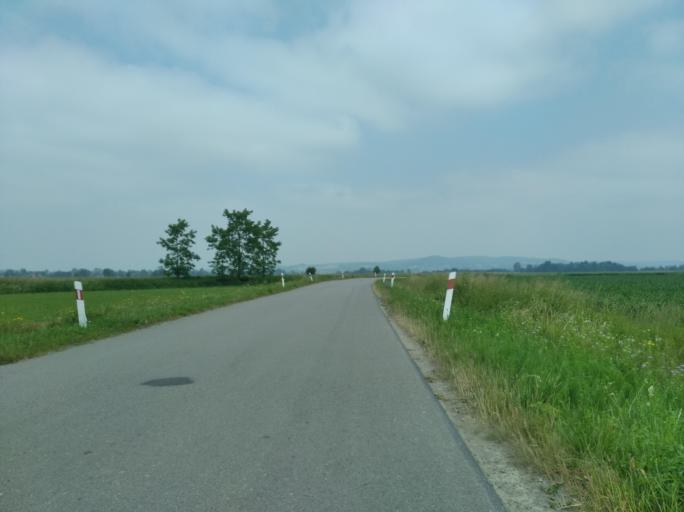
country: PL
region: Subcarpathian Voivodeship
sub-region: Powiat sanocki
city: Besko
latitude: 49.6082
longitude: 21.9552
